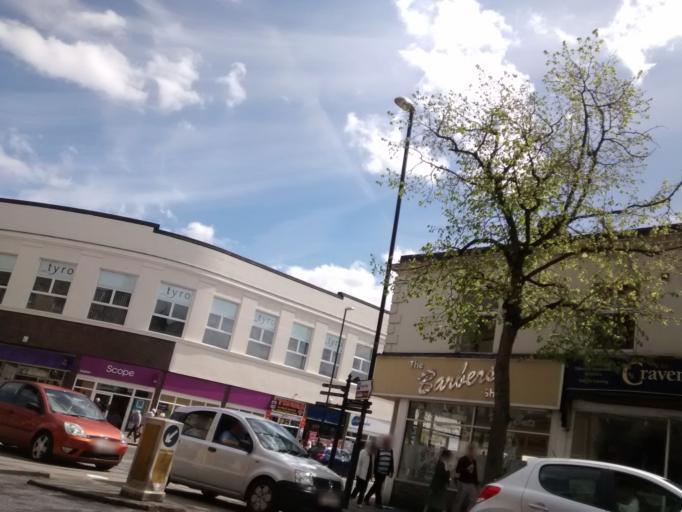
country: GB
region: England
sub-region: North Yorkshire
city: Skipton
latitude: 53.9602
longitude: -2.0179
